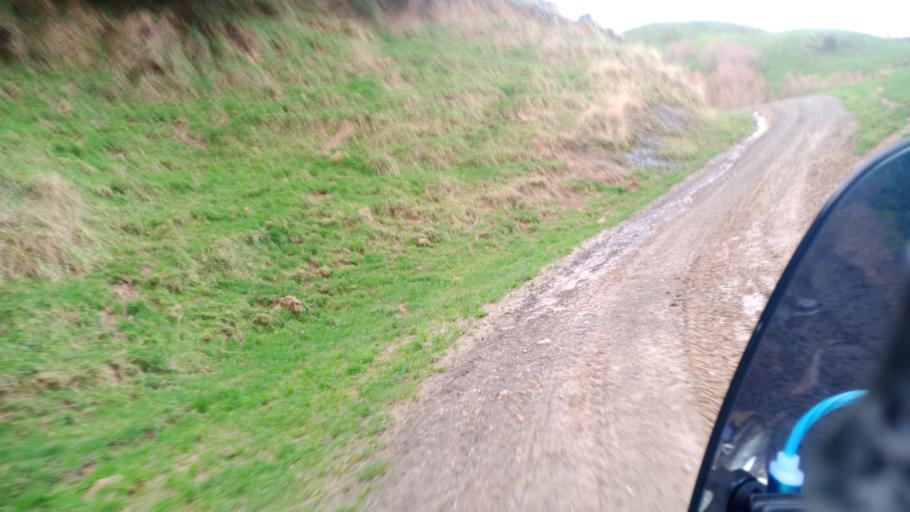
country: NZ
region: Gisborne
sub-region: Gisborne District
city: Gisborne
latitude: -38.3423
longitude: 177.9143
